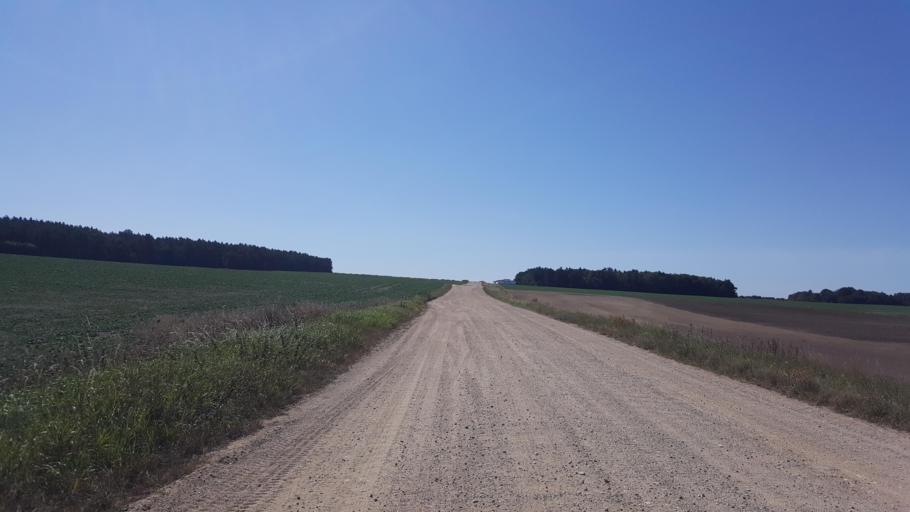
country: PL
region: Lublin Voivodeship
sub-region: Powiat bialski
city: Terespol
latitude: 52.2247
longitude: 23.5234
